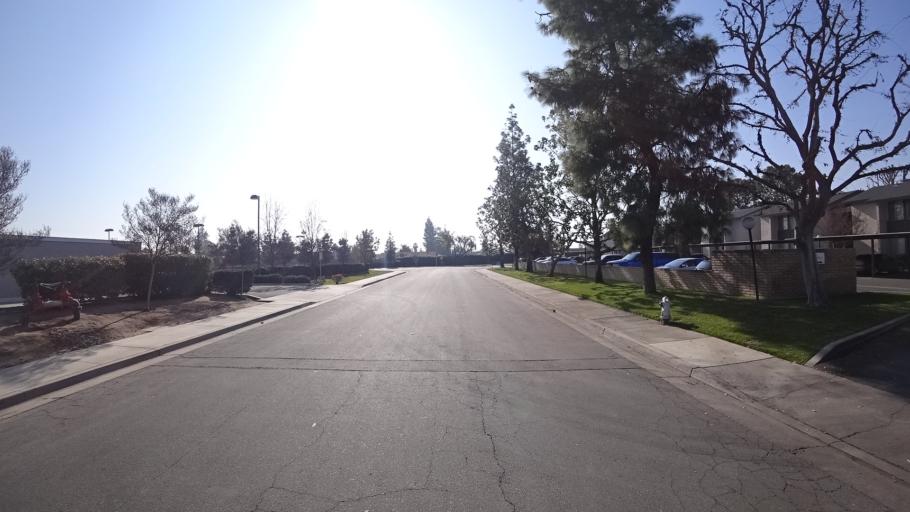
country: US
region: California
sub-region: Kern County
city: Bakersfield
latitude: 35.3385
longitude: -119.0582
